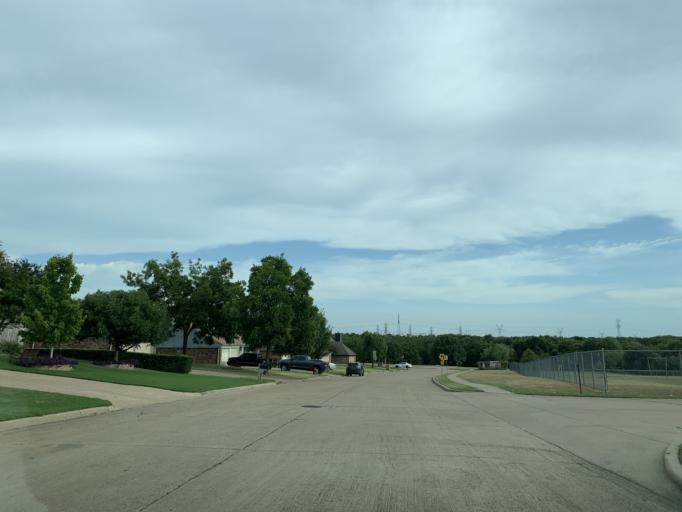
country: US
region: Texas
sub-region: Tarrant County
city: Arlington
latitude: 32.6615
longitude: -97.0456
